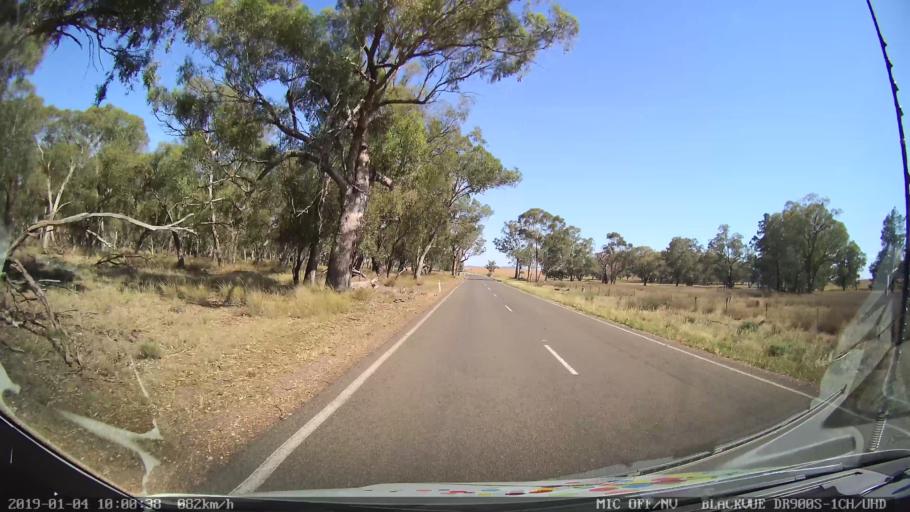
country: AU
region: New South Wales
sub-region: Cabonne
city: Canowindra
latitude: -33.4954
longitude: 148.3776
